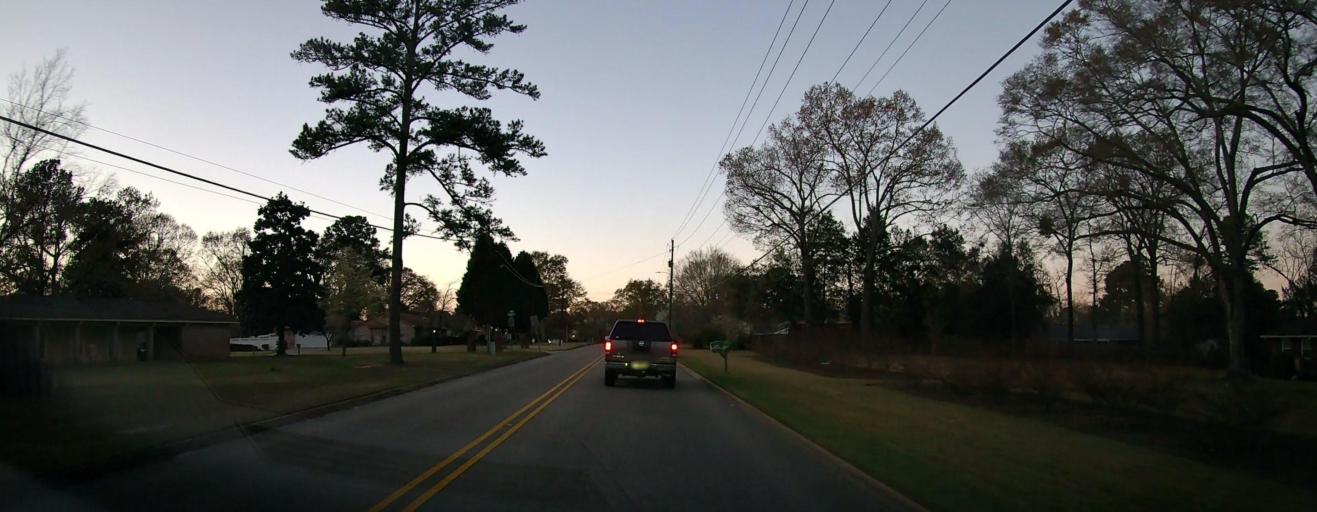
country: US
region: Alabama
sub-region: Russell County
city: Phenix City
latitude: 32.5091
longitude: -85.0197
